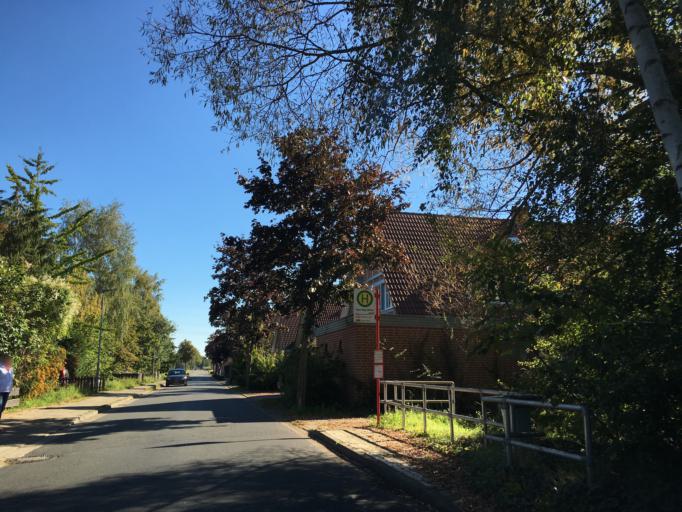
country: DE
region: Lower Saxony
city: Winsen
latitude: 53.3461
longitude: 10.2169
